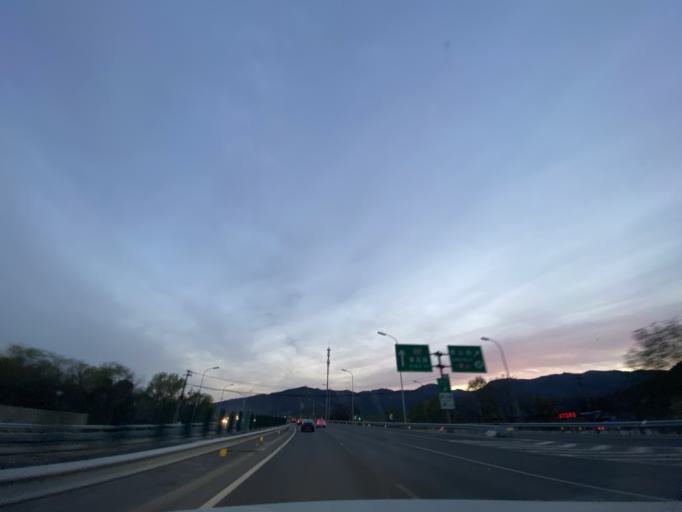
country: CN
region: Beijing
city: Xiangshan
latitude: 39.9947
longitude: 116.2206
